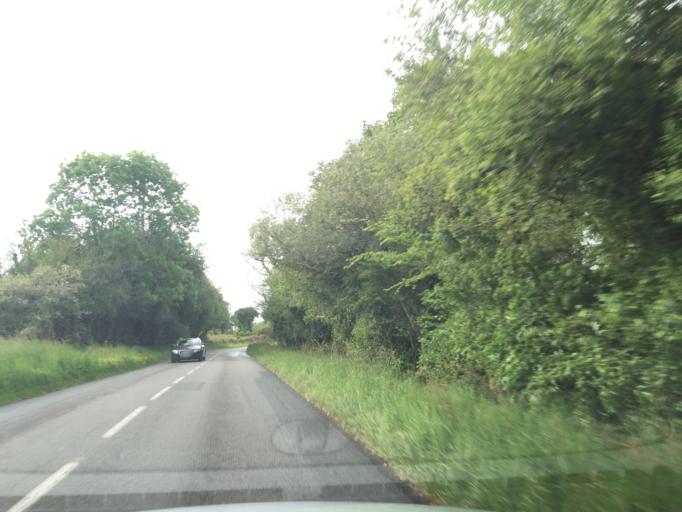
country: FR
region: Brittany
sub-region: Departement des Cotes-d'Armor
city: Crehen
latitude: 48.5789
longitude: -2.1854
